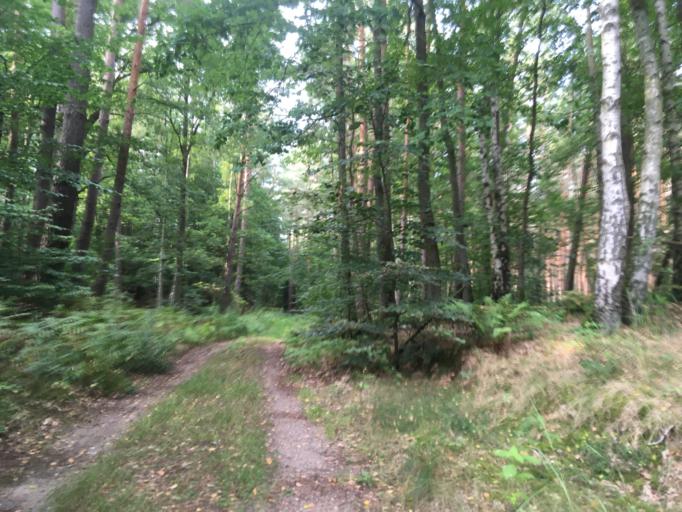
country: DE
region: Brandenburg
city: Eberswalde
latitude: 52.7972
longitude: 13.8202
